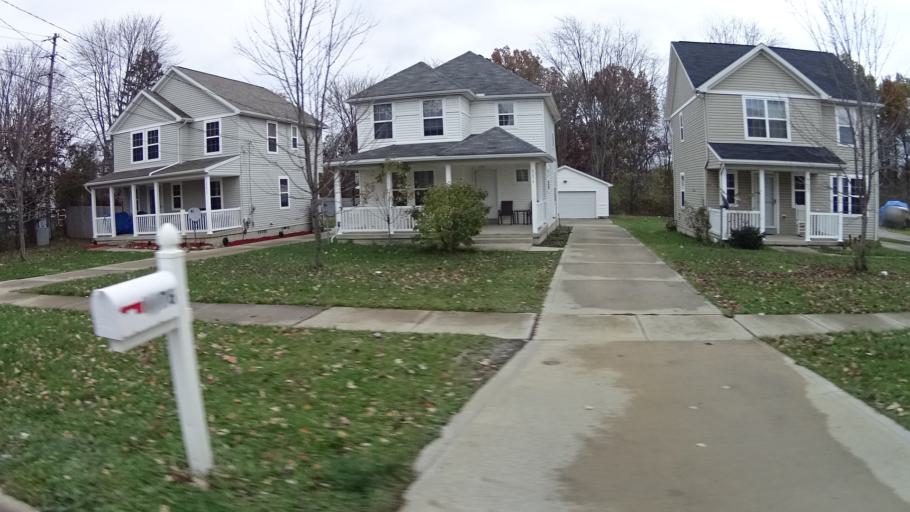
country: US
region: Ohio
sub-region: Lorain County
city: Elyria
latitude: 41.3605
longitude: -82.1162
